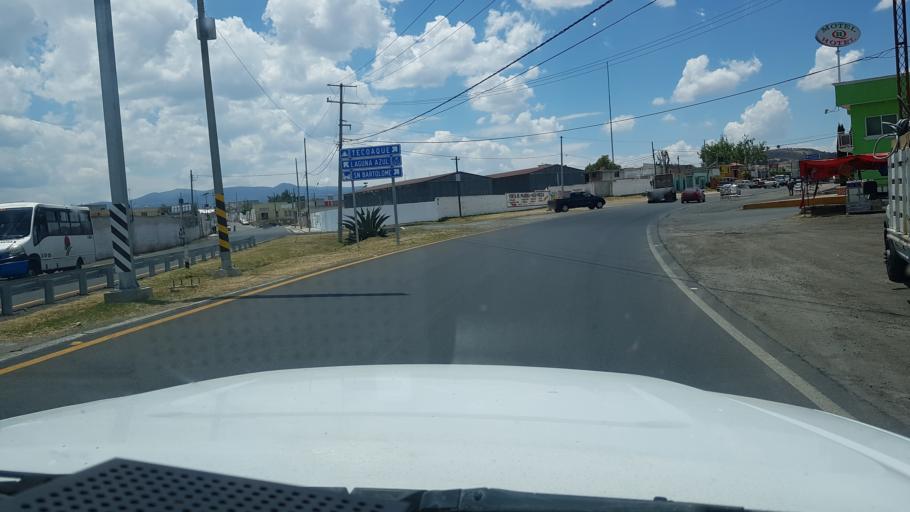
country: MX
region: Hidalgo
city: Calpulalpan
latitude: 19.5940
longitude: -98.5742
